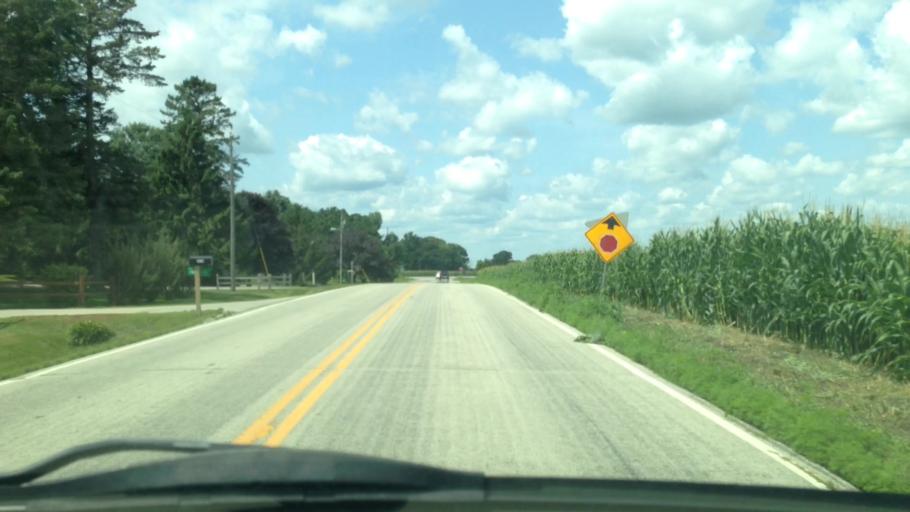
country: US
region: Minnesota
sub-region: Olmsted County
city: Rochester
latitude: 43.9532
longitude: -92.5156
